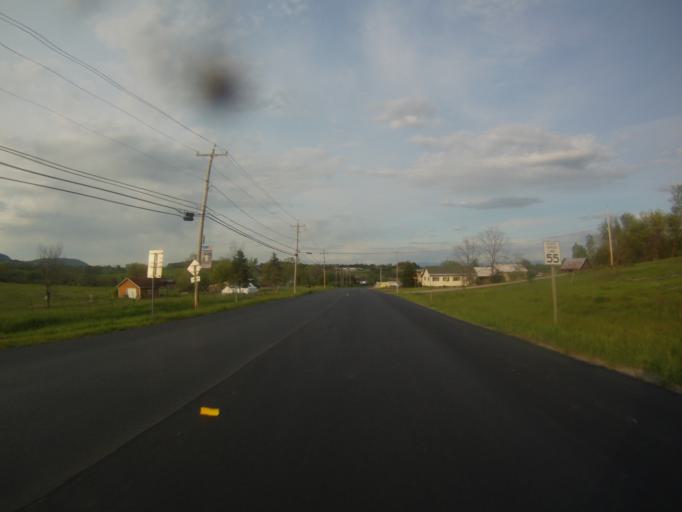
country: US
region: New York
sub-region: Essex County
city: Ticonderoga
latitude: 43.8437
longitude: -73.4487
